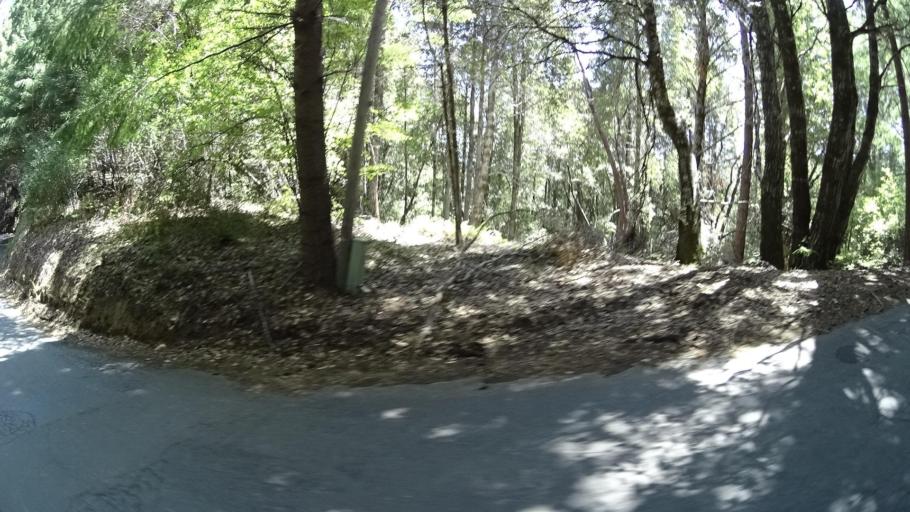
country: US
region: California
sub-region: Humboldt County
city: Redway
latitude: 40.0965
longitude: -123.9513
